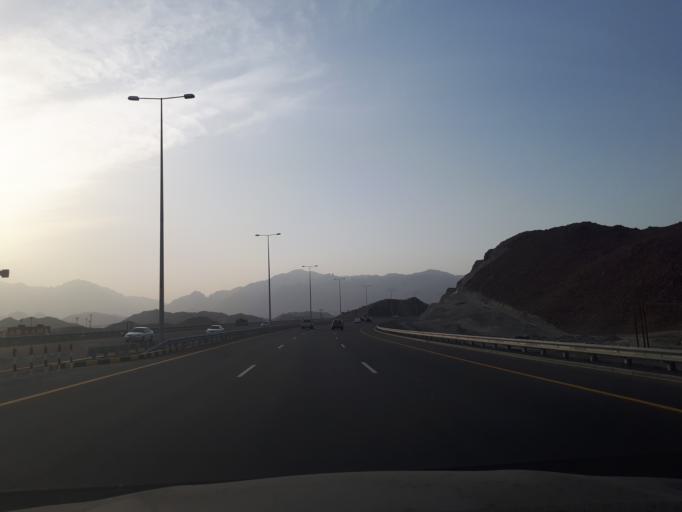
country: OM
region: Muhafazat ad Dakhiliyah
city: Bidbid
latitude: 23.3488
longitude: 58.0930
